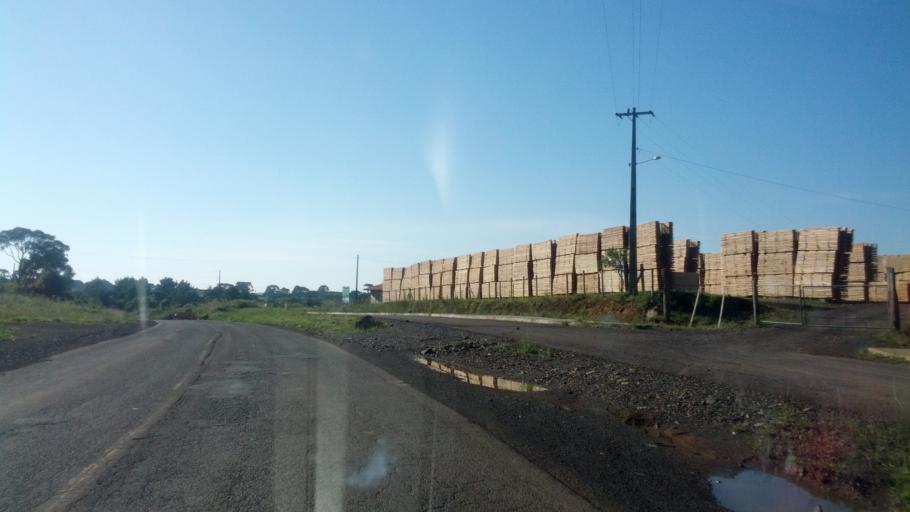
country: BR
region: Santa Catarina
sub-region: Lages
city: Lages
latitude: -27.9471
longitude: -50.5048
